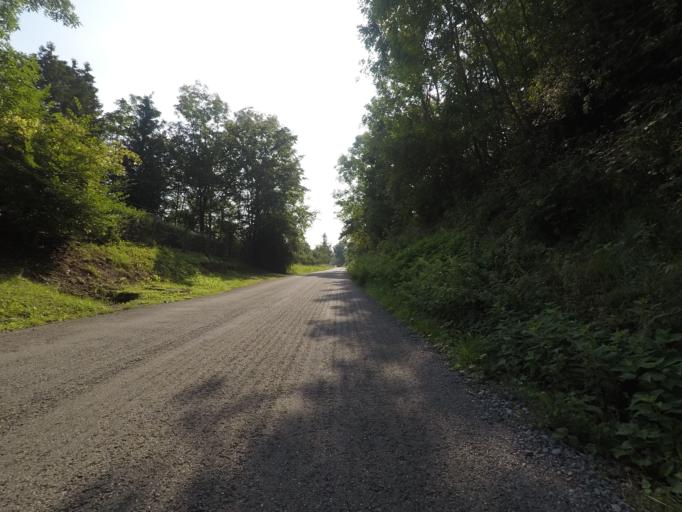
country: DE
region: Baden-Wuerttemberg
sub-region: Regierungsbezirk Stuttgart
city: Weinstadt-Endersbach
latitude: 48.8059
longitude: 9.4005
